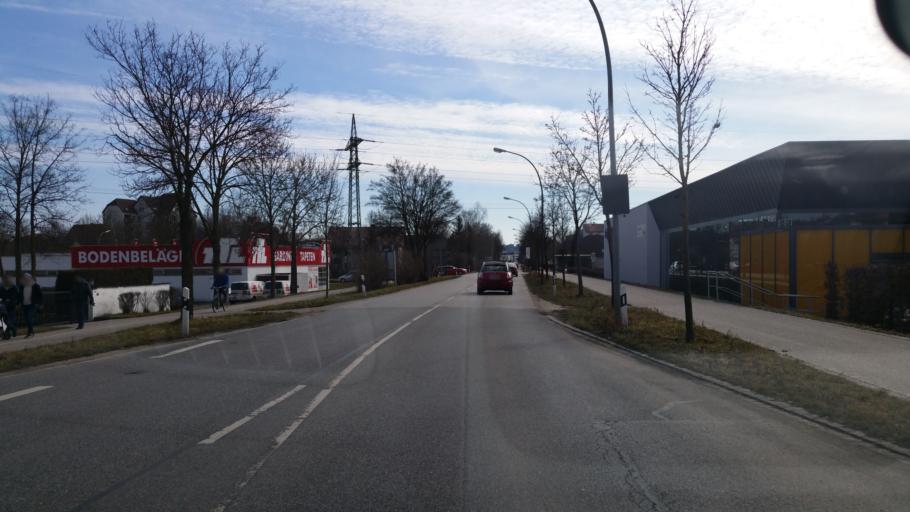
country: DE
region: Bavaria
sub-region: Lower Bavaria
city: Ergolding
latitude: 48.5596
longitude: 12.1357
